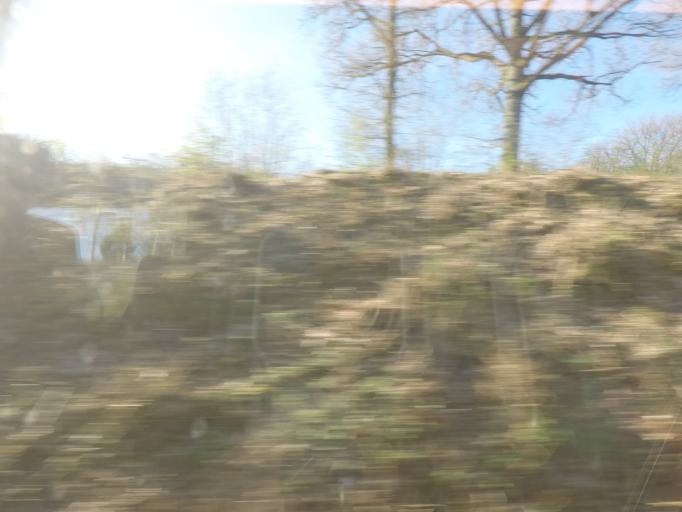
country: BE
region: Wallonia
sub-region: Province de Namur
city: Ciney
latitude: 50.2660
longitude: 5.1680
